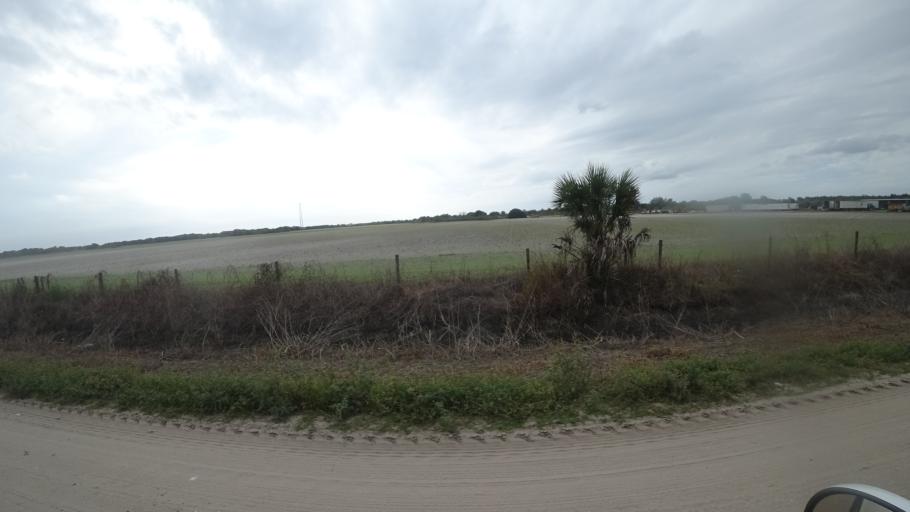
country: US
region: Florida
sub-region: Sarasota County
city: Warm Mineral Springs
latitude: 27.2780
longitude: -82.1699
